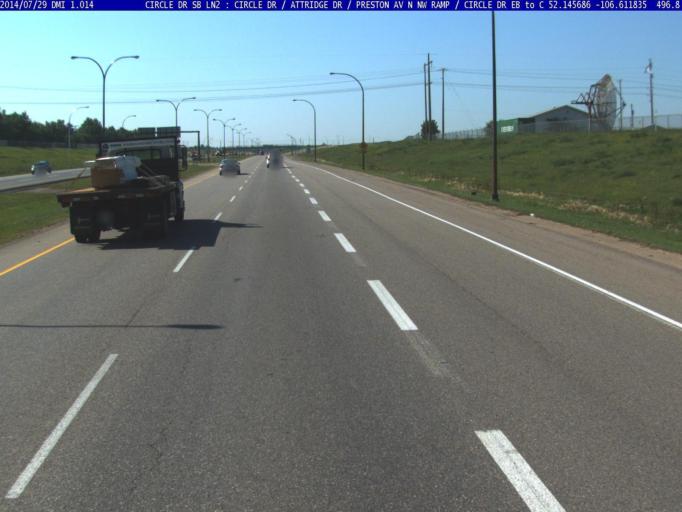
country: CA
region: Saskatchewan
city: Saskatoon
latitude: 52.1457
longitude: -106.6118
